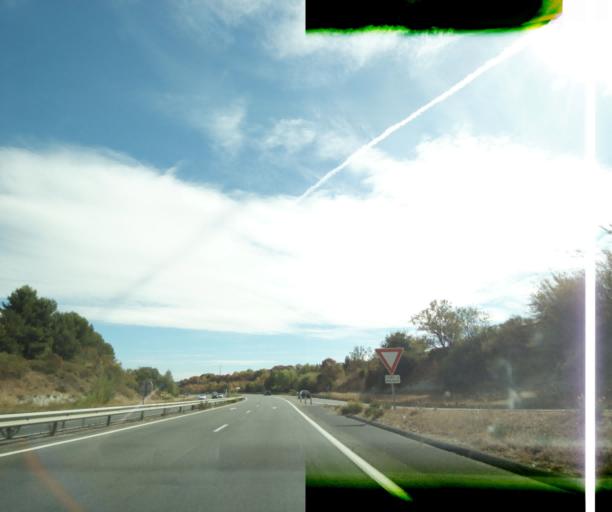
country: FR
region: Languedoc-Roussillon
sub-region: Departement de l'Herault
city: Juvignac
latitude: 43.6094
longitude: 3.8045
